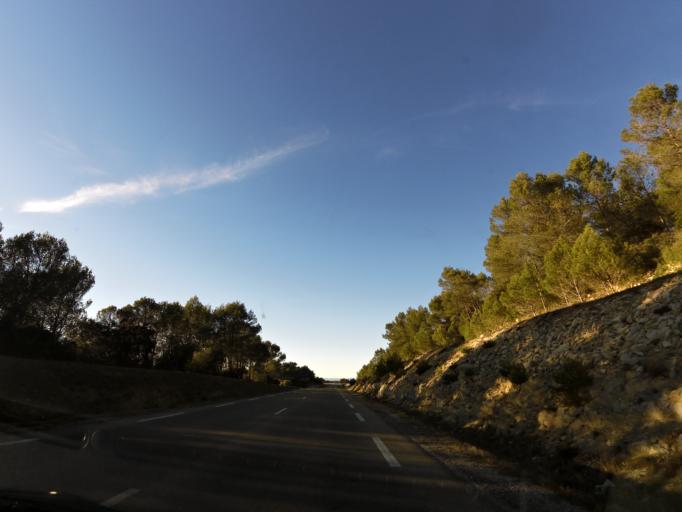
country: FR
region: Languedoc-Roussillon
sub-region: Departement du Gard
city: Aubais
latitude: 43.7805
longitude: 4.1358
